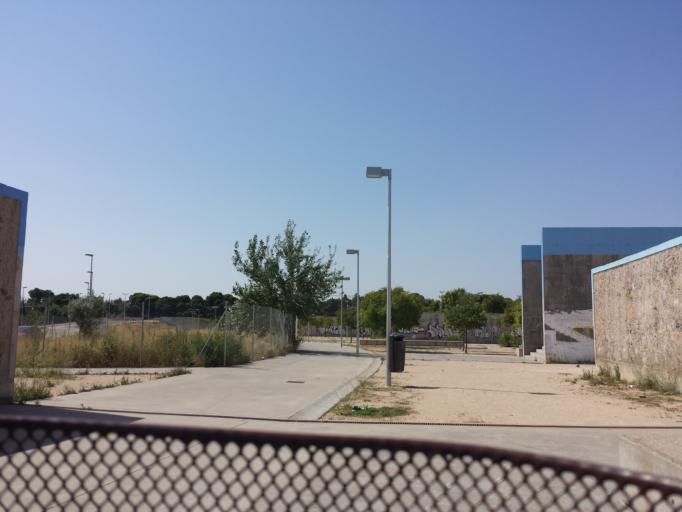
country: ES
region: Aragon
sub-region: Provincia de Zaragoza
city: Oliver-Valdefierro, Oliver, Valdefierro
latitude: 41.6372
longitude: -0.9294
